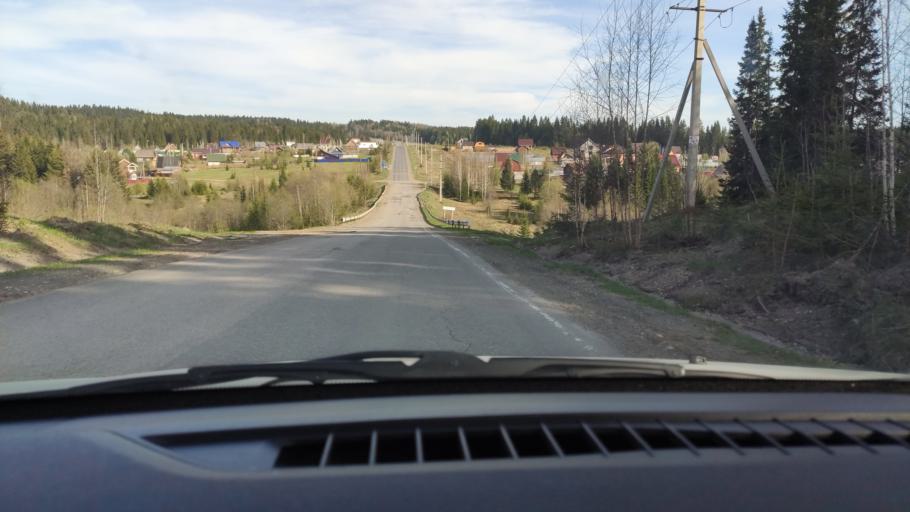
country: RU
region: Perm
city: Novyye Lyady
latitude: 57.9381
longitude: 56.6252
